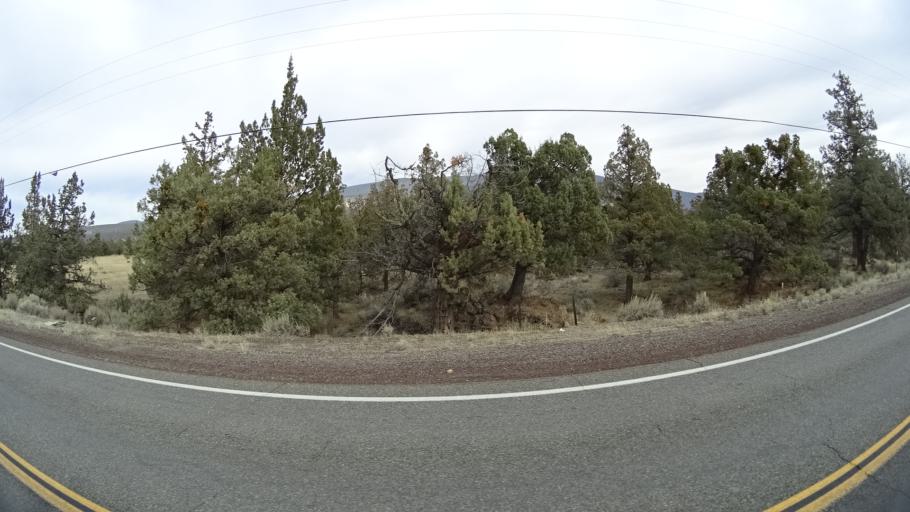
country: US
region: California
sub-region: Siskiyou County
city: Weed
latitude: 41.5902
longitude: -122.3040
